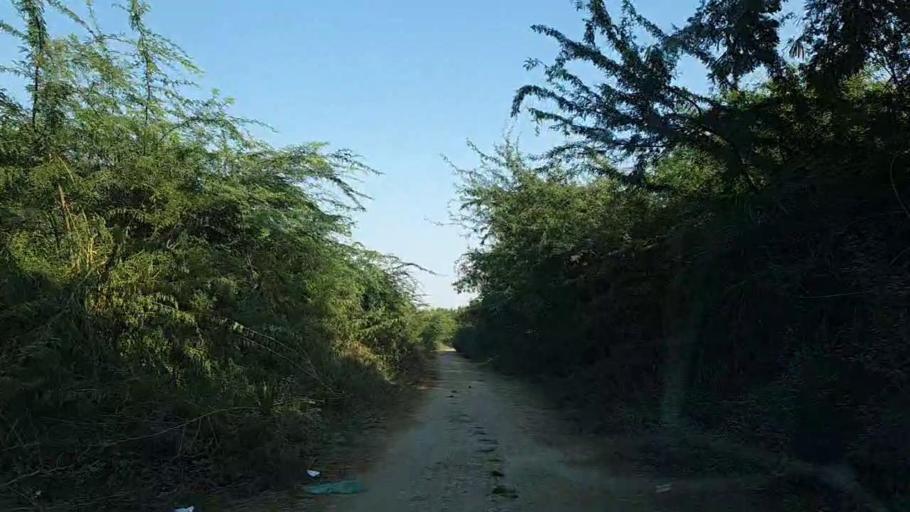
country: PK
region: Sindh
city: Chuhar Jamali
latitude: 24.5717
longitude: 68.0319
